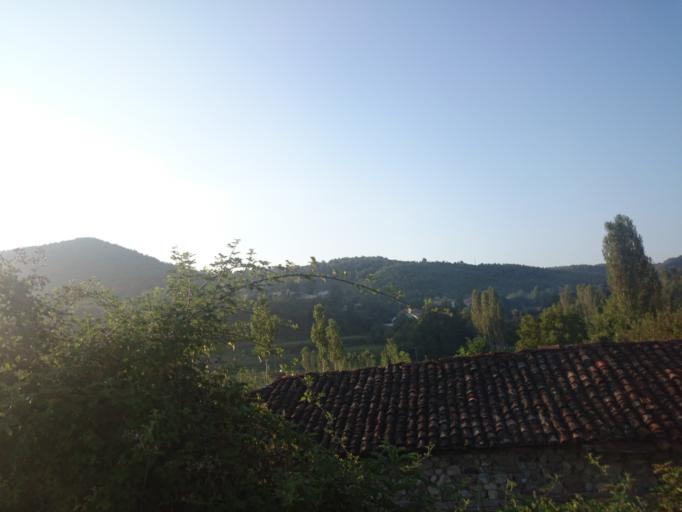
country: AL
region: Diber
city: Peshkopi
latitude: 41.6721
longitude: 20.4182
